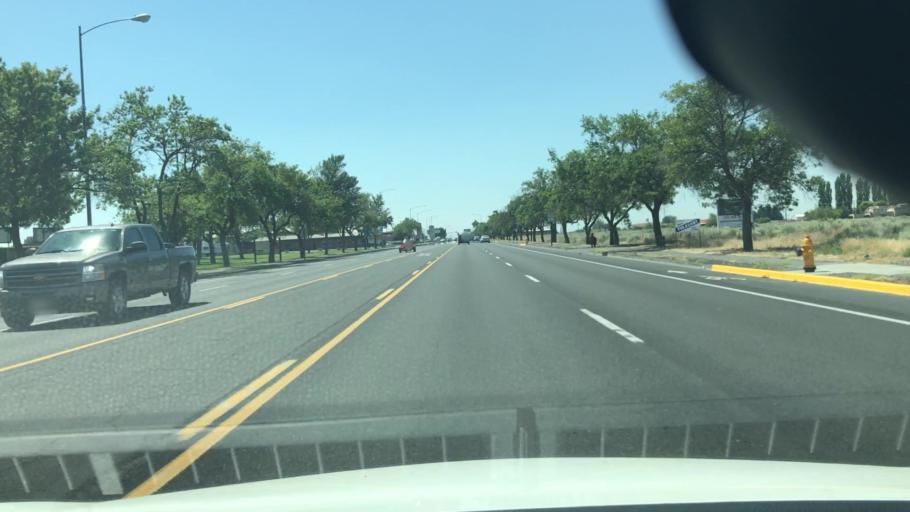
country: US
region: Washington
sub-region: Grant County
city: Cascade Valley
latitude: 47.1071
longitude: -119.3077
